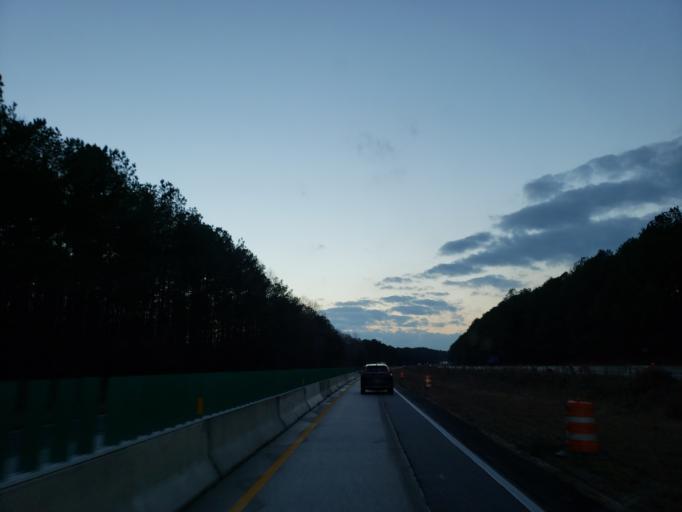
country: US
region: Georgia
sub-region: Carroll County
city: Temple
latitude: 33.6986
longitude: -85.0723
